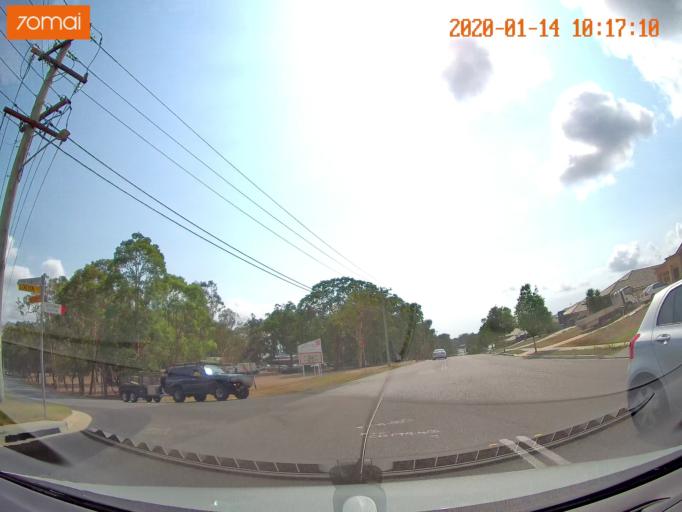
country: AU
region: New South Wales
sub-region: Lake Macquarie Shire
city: Dora Creek
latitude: -33.1087
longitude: 151.5065
